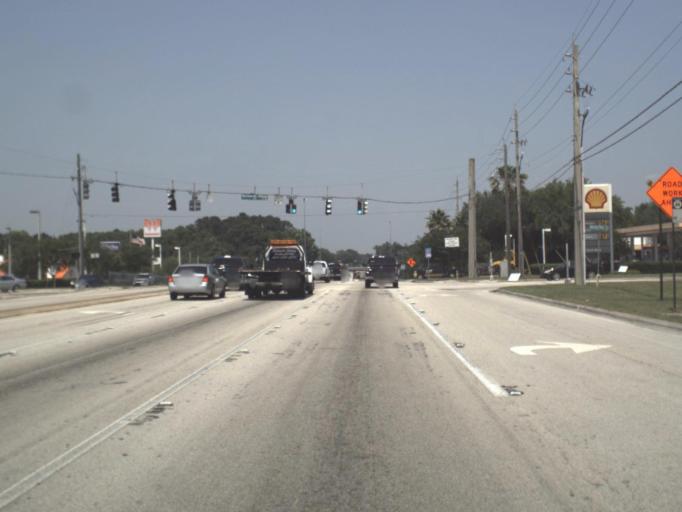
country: US
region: Florida
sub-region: Clay County
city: Bellair-Meadowbrook Terrace
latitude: 30.2946
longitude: -81.7769
